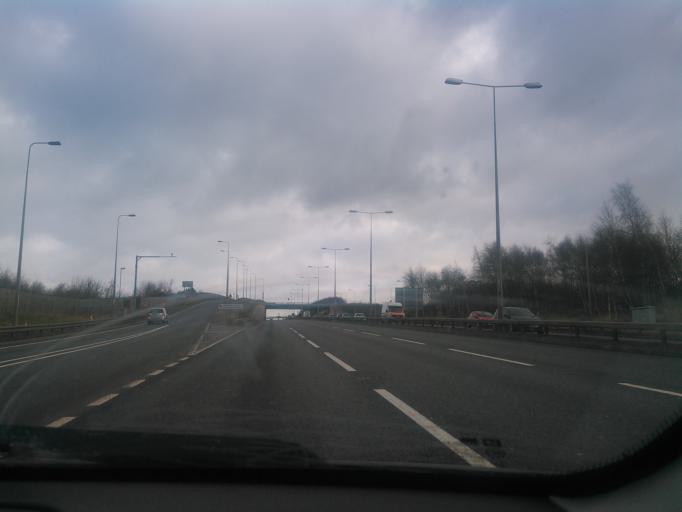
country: GB
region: England
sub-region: Stoke-on-Trent
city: Stoke-on-Trent
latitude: 52.9904
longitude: -2.1753
